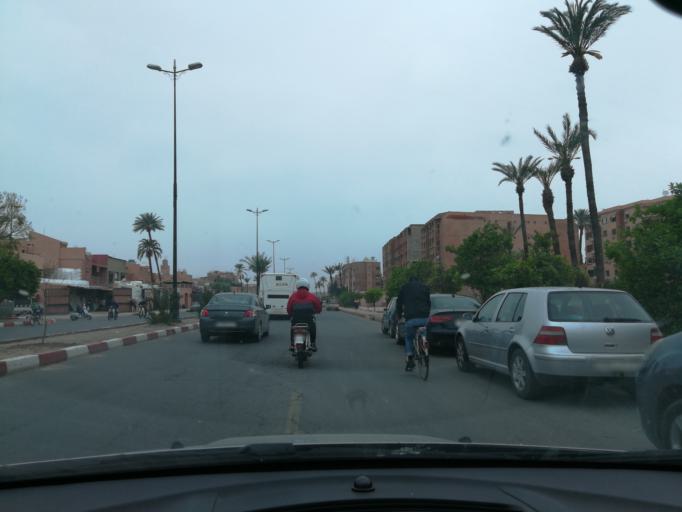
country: MA
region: Marrakech-Tensift-Al Haouz
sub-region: Marrakech
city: Marrakesh
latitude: 31.6415
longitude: -8.0063
